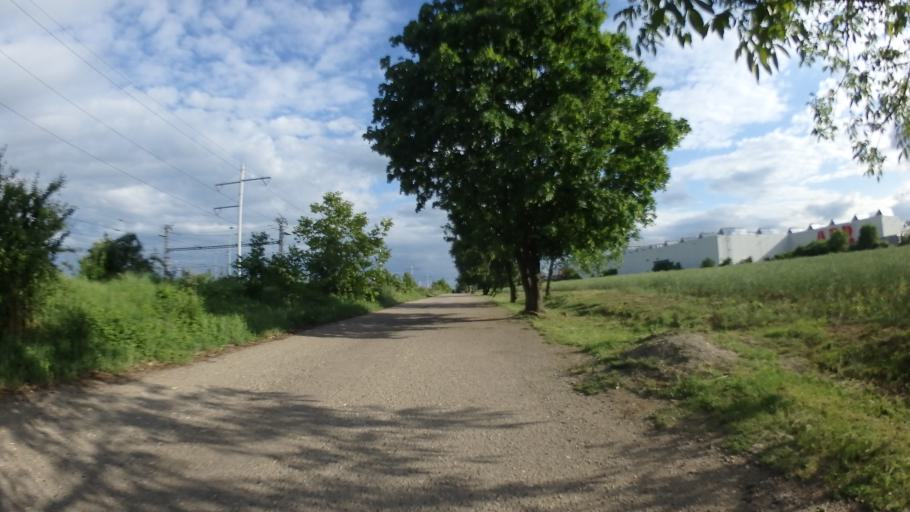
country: CZ
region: South Moravian
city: Moravany
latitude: 49.1573
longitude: 16.6064
